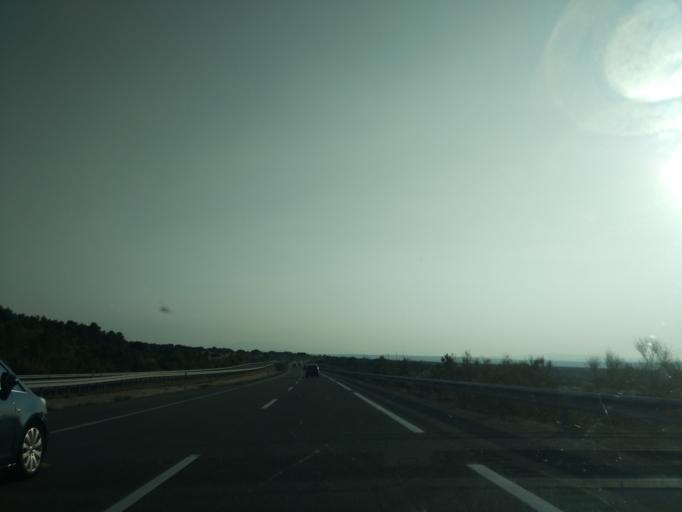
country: ES
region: Castille and Leon
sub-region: Provincia de Avila
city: Ojos-Albos
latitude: 40.7329
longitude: -4.5053
